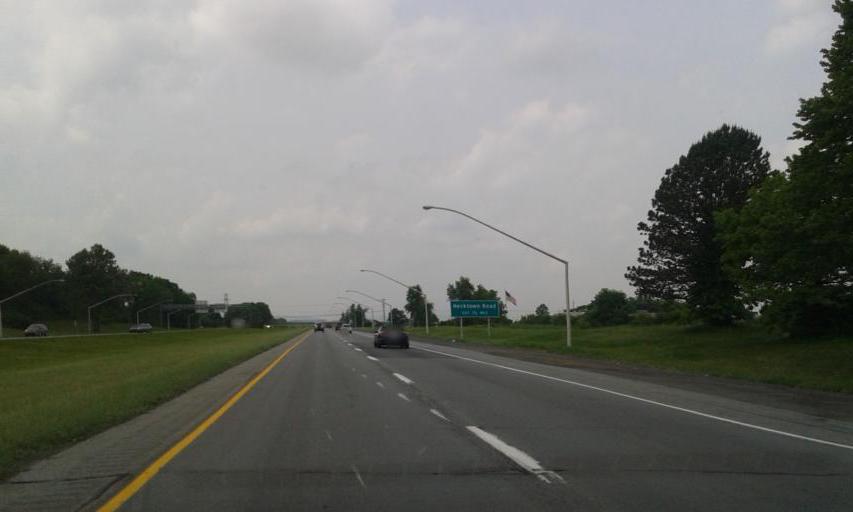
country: US
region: Pennsylvania
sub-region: Northampton County
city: Palmer Heights
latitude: 40.6903
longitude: -75.2889
